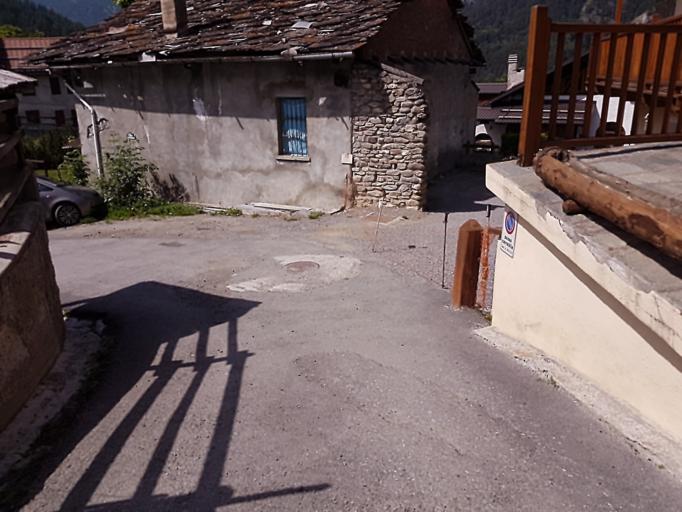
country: IT
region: Piedmont
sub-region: Provincia di Torino
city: Cesana Torinese
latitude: 44.9704
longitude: 6.8009
